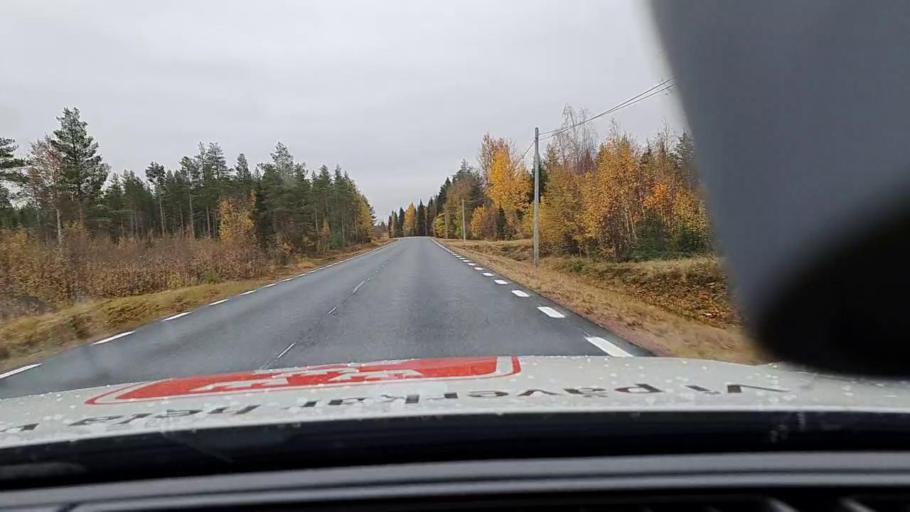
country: FI
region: Lapland
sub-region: Torniolaakso
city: Ylitornio
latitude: 66.1516
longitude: 23.8793
